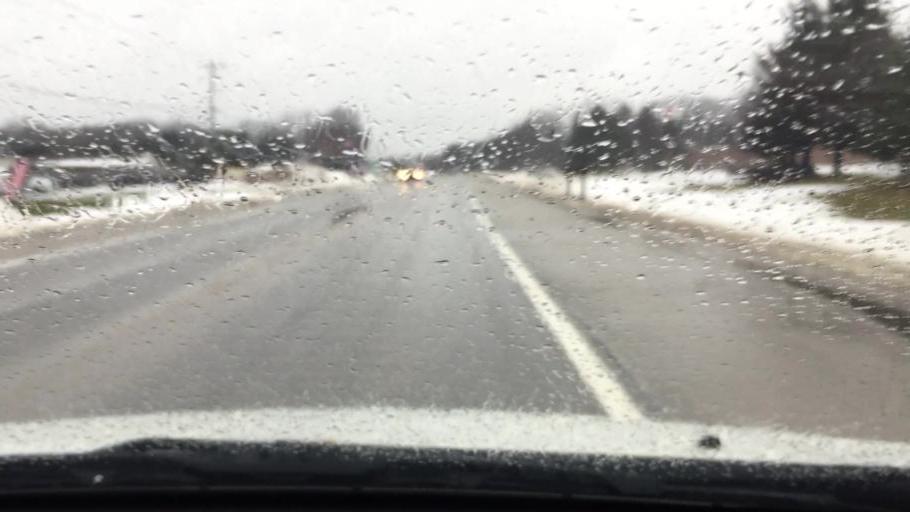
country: US
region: Michigan
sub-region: Charlevoix County
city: Charlevoix
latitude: 45.2979
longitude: -85.2553
